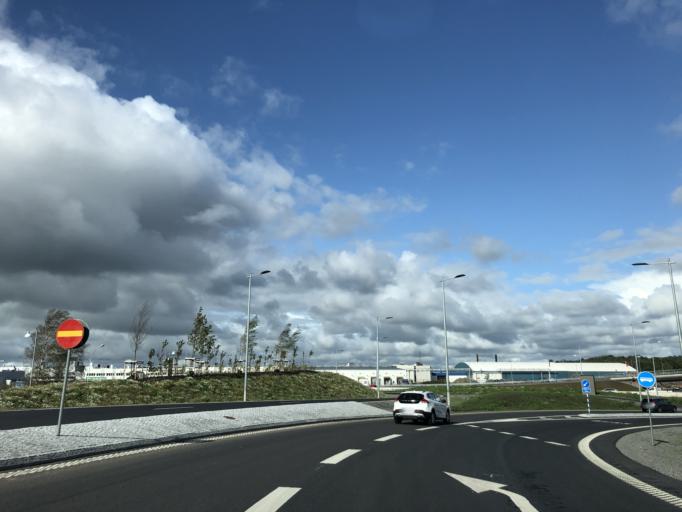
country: SE
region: Vaestra Goetaland
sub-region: Goteborg
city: Torslanda
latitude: 57.7114
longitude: 11.8388
